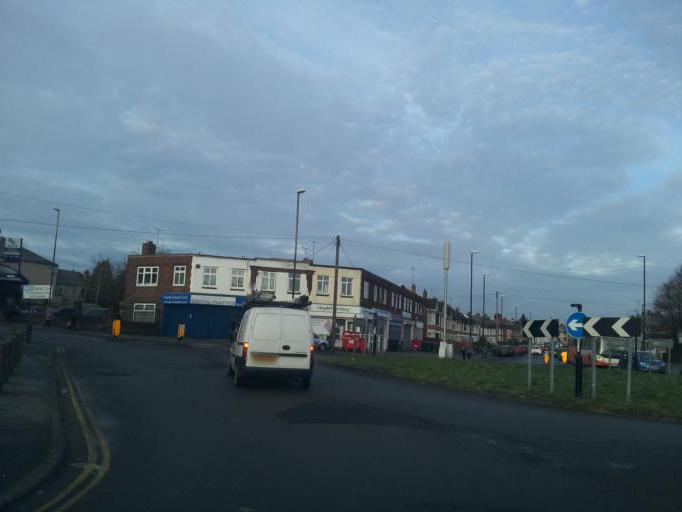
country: GB
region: England
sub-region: Coventry
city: Coventry
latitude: 52.4203
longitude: -1.4689
